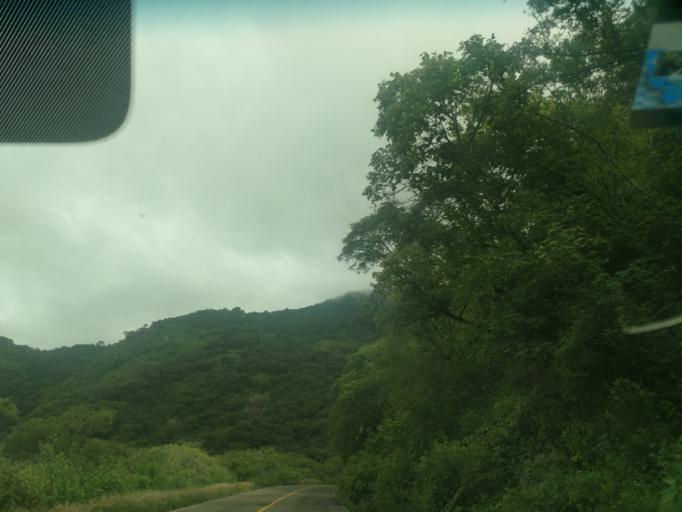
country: MX
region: Jalisco
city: El Salto
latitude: 20.3656
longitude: -104.5806
